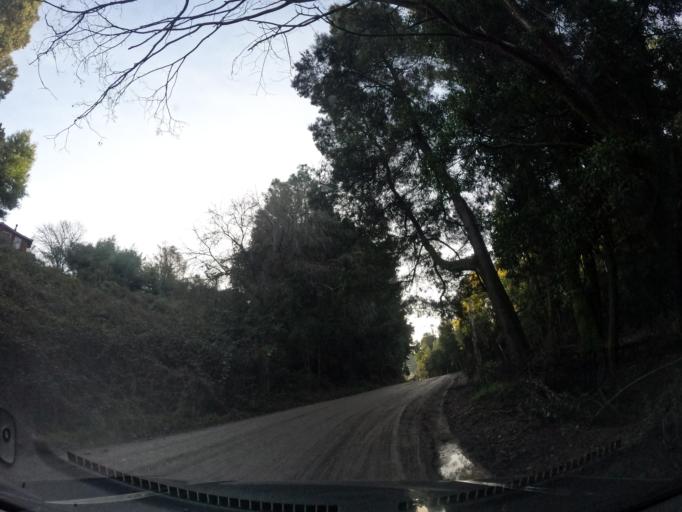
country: CL
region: Biobio
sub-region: Provincia de Concepcion
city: Concepcion
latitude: -36.8580
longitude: -73.0010
